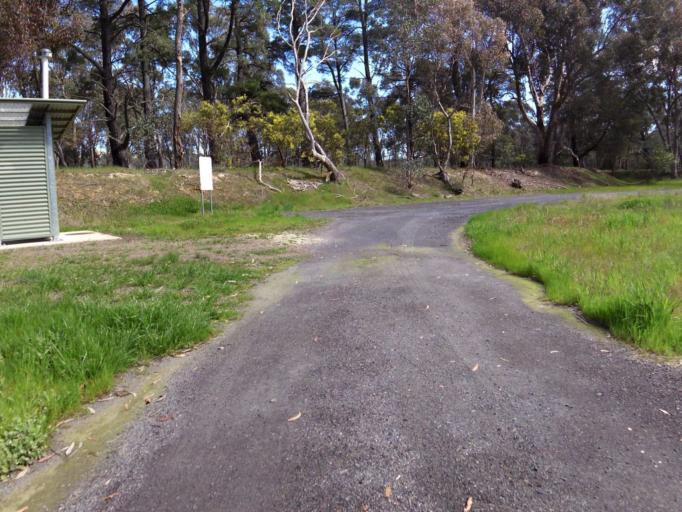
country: AU
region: Victoria
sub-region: Murrindindi
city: Alexandra
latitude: -37.1547
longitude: 145.6571
